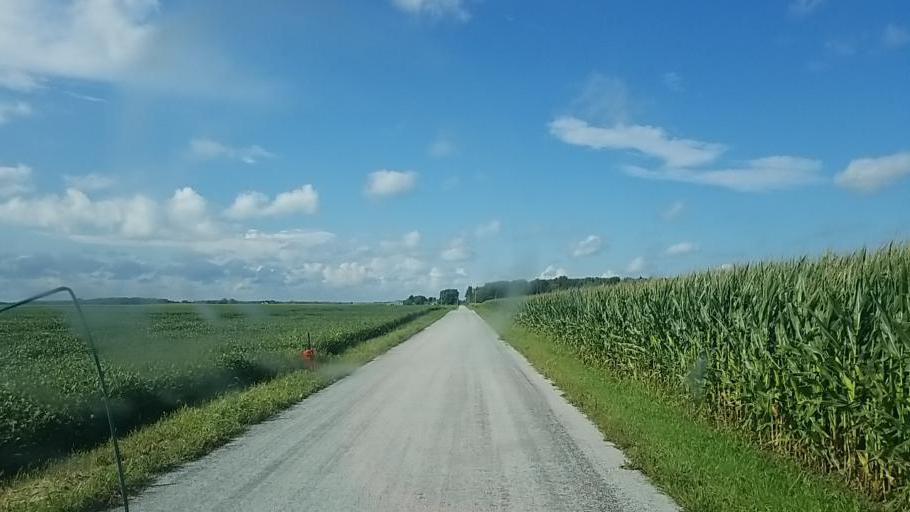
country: US
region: Ohio
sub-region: Hardin County
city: Kenton
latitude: 40.6848
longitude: -83.5309
